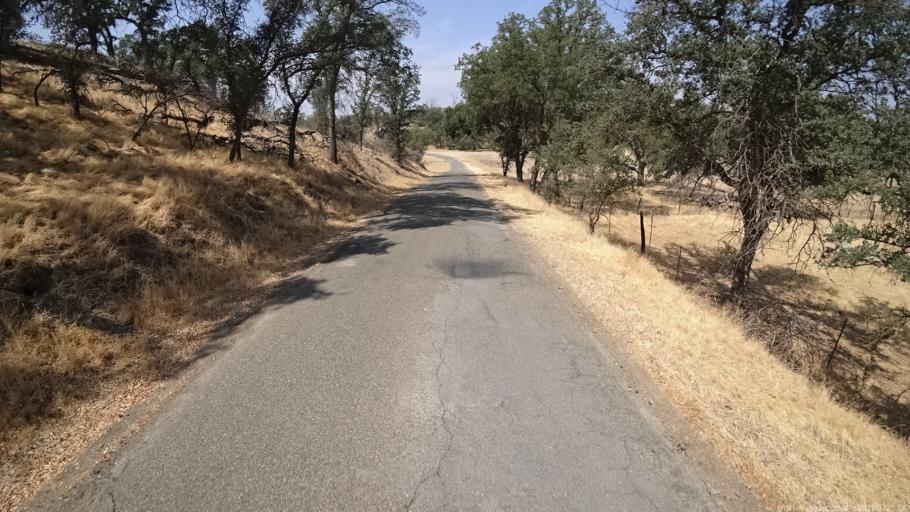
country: US
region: California
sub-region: San Luis Obispo County
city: Shandon
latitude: 35.8789
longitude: -120.3952
